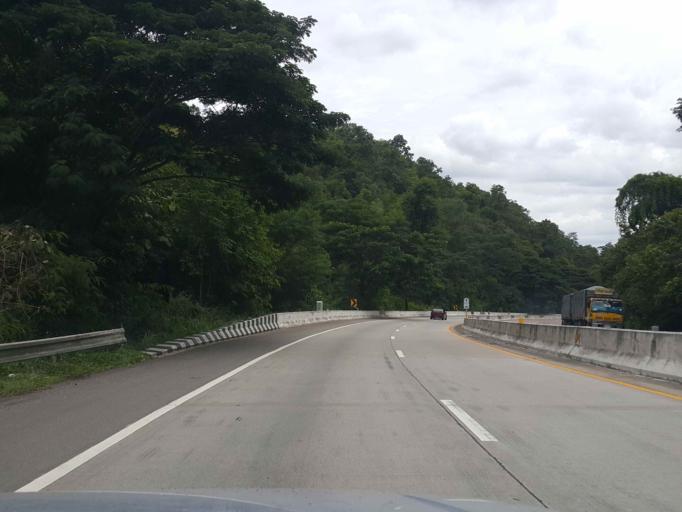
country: TH
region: Lamphun
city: Mae Tha
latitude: 18.4062
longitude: 99.2121
